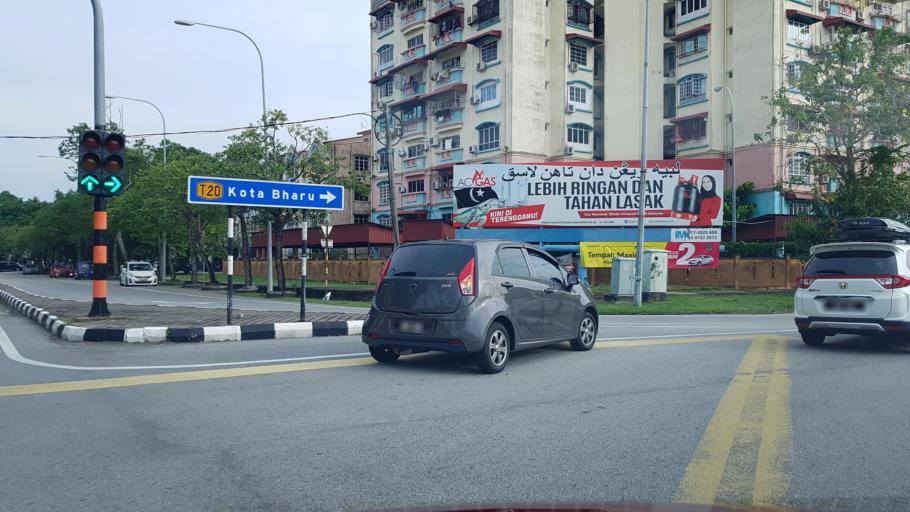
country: MY
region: Terengganu
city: Kuala Terengganu
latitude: 5.3265
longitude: 103.1387
